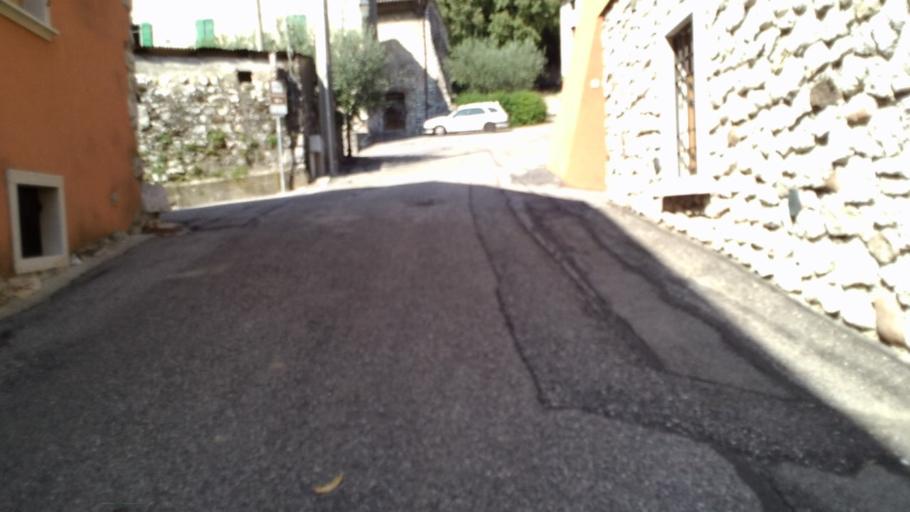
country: IT
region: Veneto
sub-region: Provincia di Verona
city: Dolce
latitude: 45.6251
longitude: 10.8595
